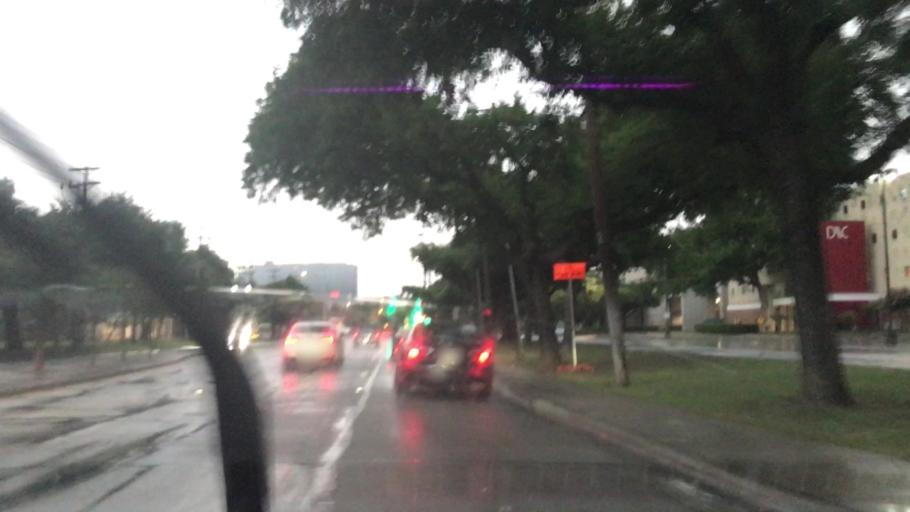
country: US
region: Texas
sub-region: Dallas County
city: Dallas
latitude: 32.8024
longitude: -96.8275
